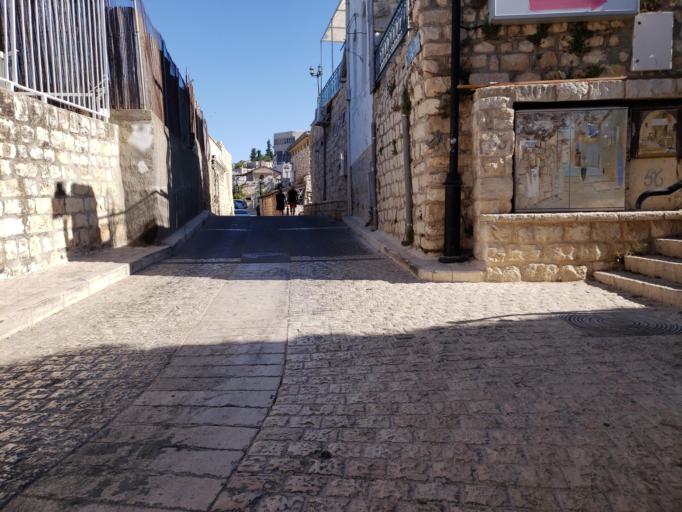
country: IL
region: Northern District
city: Safed
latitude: 32.9650
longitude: 35.4942
